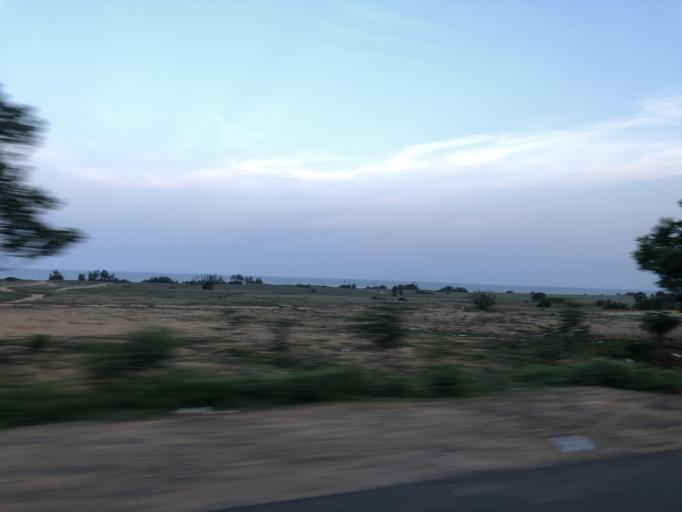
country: IN
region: Tamil Nadu
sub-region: Kancheepuram
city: Mamallapuram
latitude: 12.7533
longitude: 80.2420
